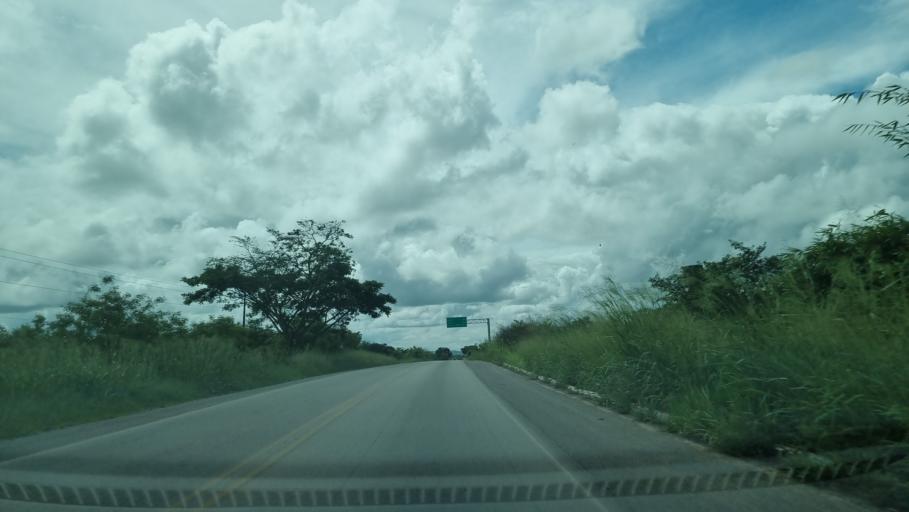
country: BR
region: Pernambuco
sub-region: Caruaru
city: Caruaru
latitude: -8.3438
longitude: -35.9831
